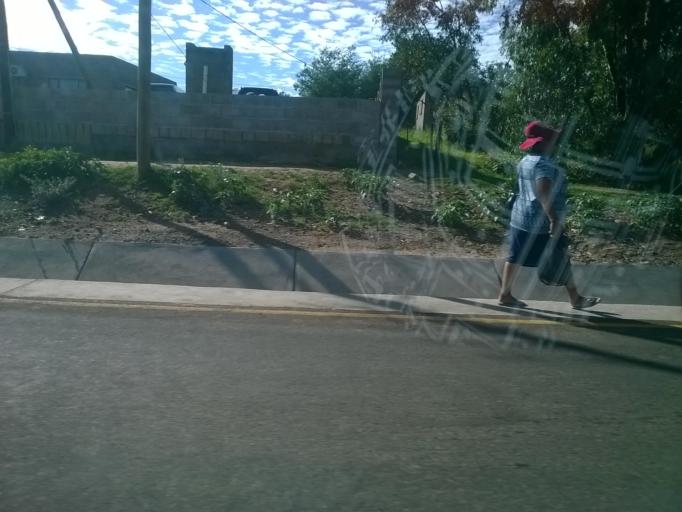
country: LS
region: Berea
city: Teyateyaneng
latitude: -29.1465
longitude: 27.7579
